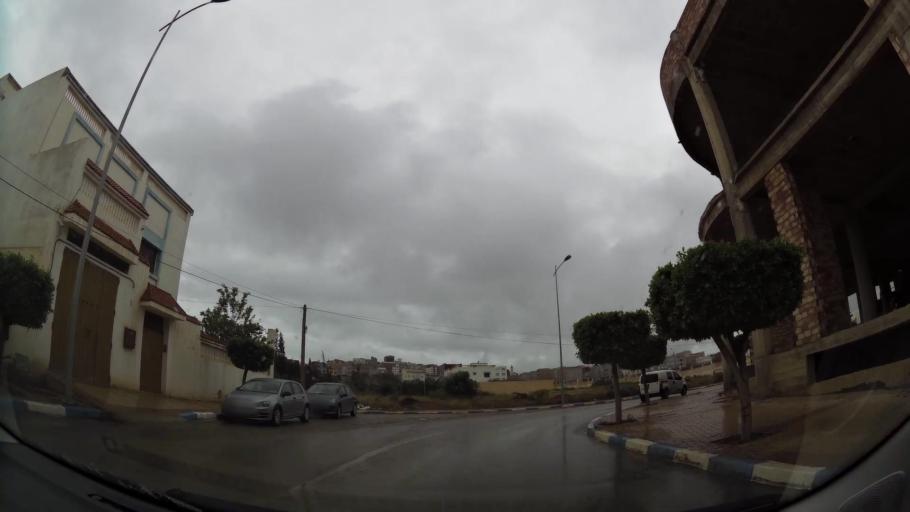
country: MA
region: Taza-Al Hoceima-Taounate
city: Imzourene
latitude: 35.1352
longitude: -3.8488
